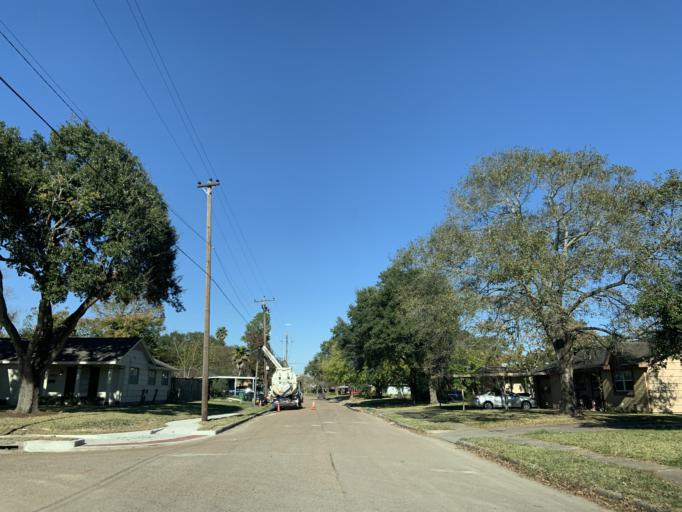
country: US
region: Texas
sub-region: Harris County
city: Bellaire
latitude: 29.6959
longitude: -95.5056
